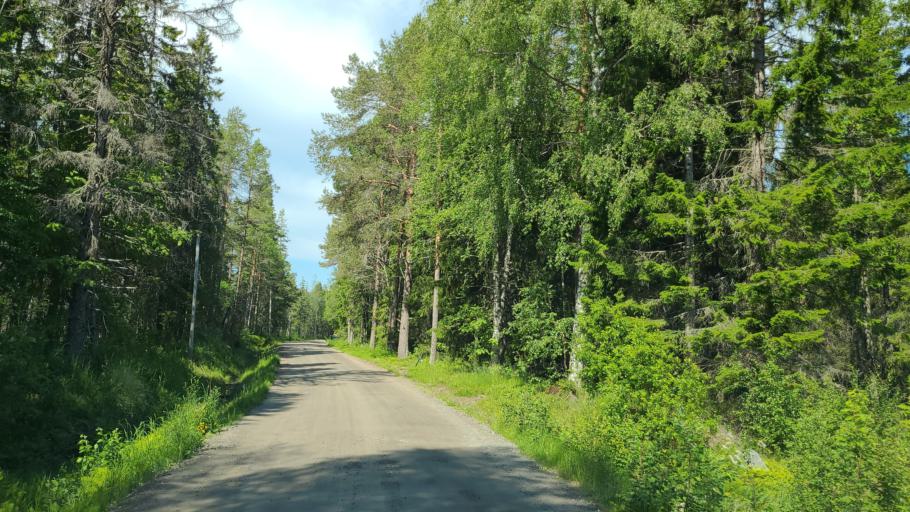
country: SE
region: Vaesterbotten
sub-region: Robertsfors Kommun
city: Robertsfors
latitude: 64.1449
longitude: 20.9600
